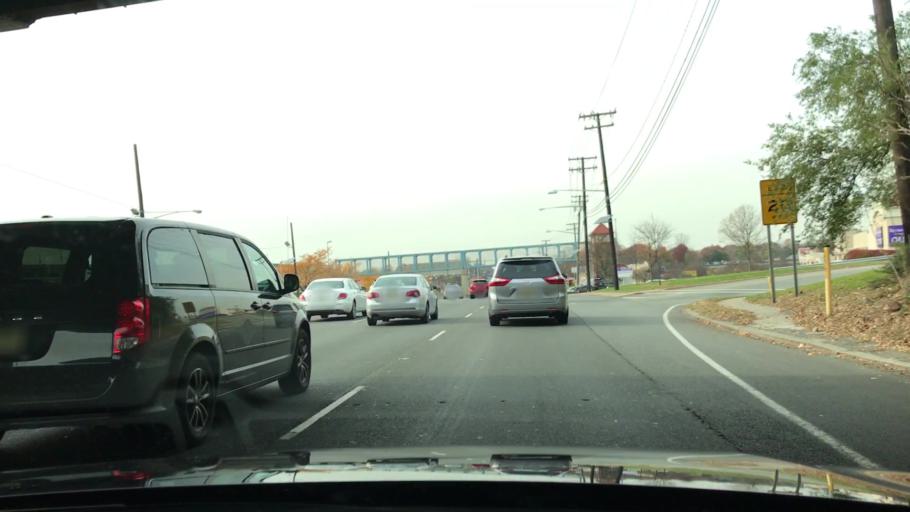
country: US
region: New Jersey
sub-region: Bergen County
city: Maywood
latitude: 40.9163
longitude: -74.0548
